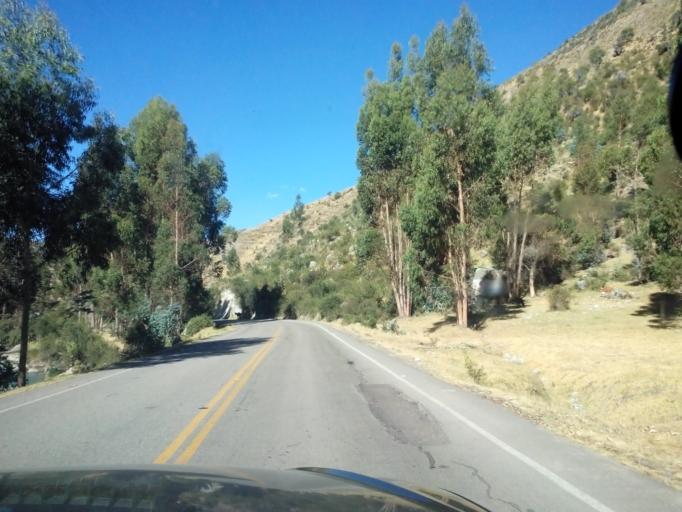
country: PE
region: Ayacucho
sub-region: Provincia de Huamanga
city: Vinchos
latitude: -13.3560
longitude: -74.4105
